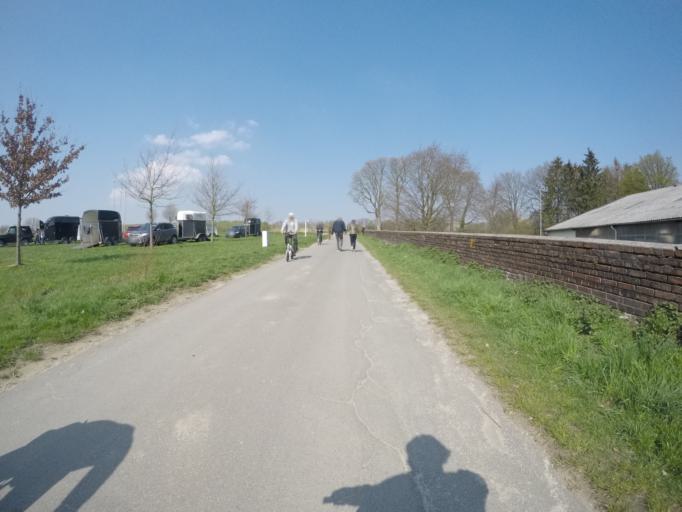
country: DE
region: North Rhine-Westphalia
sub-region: Regierungsbezirk Detmold
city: Bielefeld
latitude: 52.0586
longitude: 8.5863
